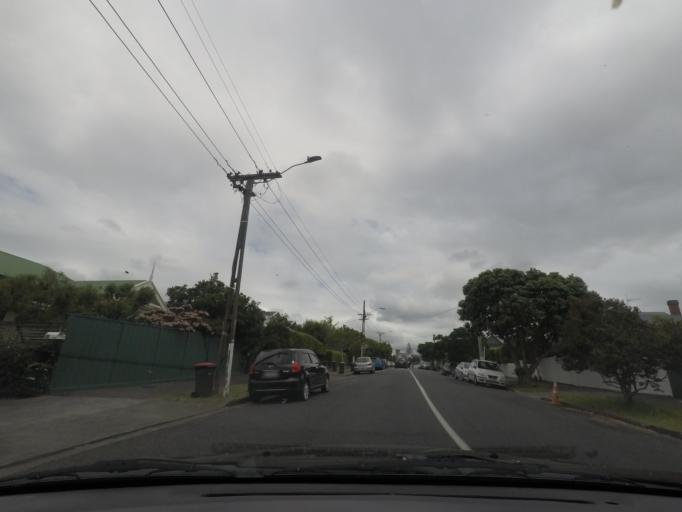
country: NZ
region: Auckland
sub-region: Auckland
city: Auckland
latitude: -36.8685
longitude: 174.7838
